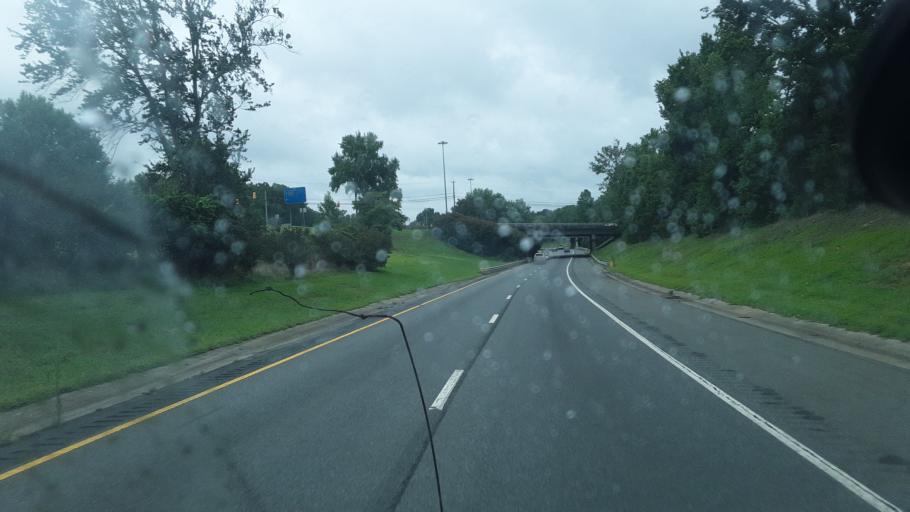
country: US
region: North Carolina
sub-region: Randolph County
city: Asheboro
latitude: 35.7099
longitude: -79.8287
